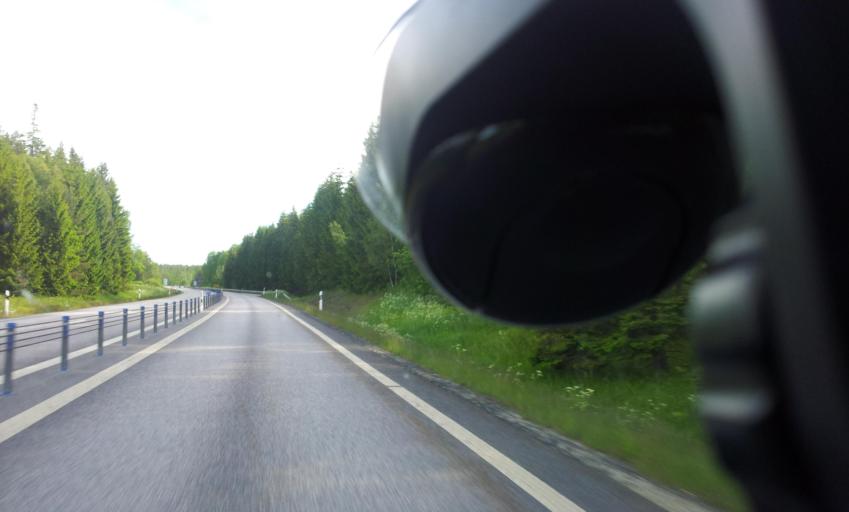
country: SE
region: OEstergoetland
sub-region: Valdemarsviks Kommun
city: Valdemarsvik
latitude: 58.1810
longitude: 16.5365
